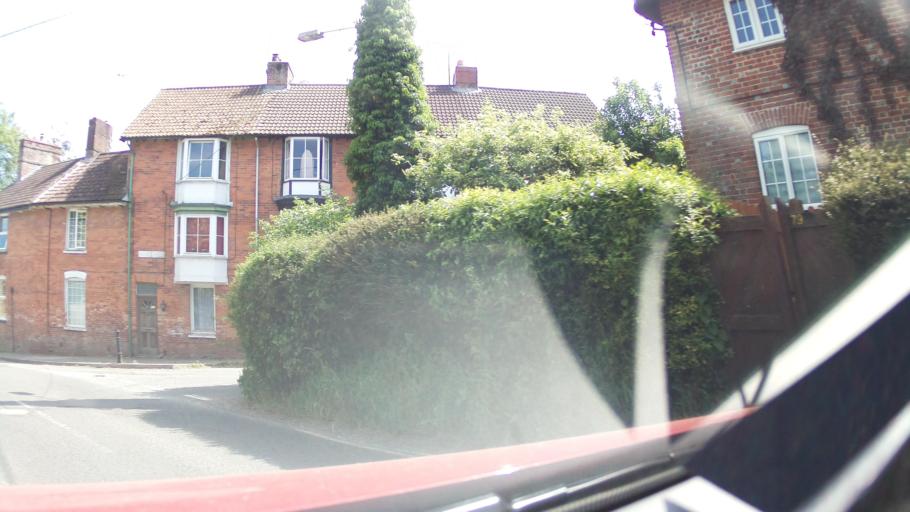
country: GB
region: England
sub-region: Wiltshire
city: Pewsey
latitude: 51.3417
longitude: -1.7685
